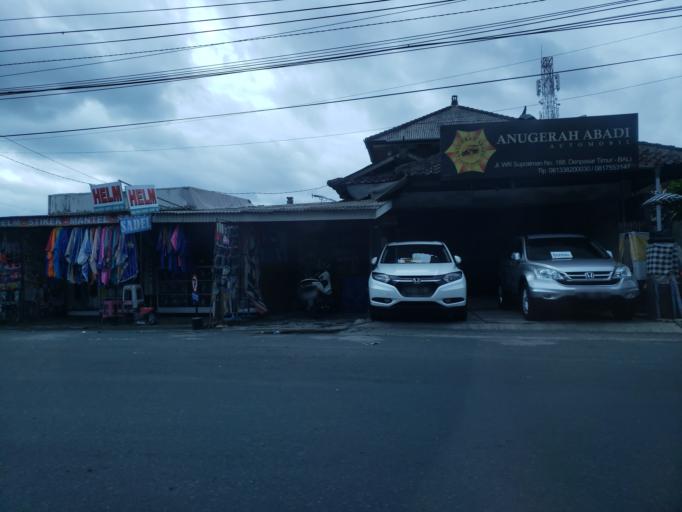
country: ID
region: Bali
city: Dajan Tangluk
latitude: -8.6479
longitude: 115.2420
